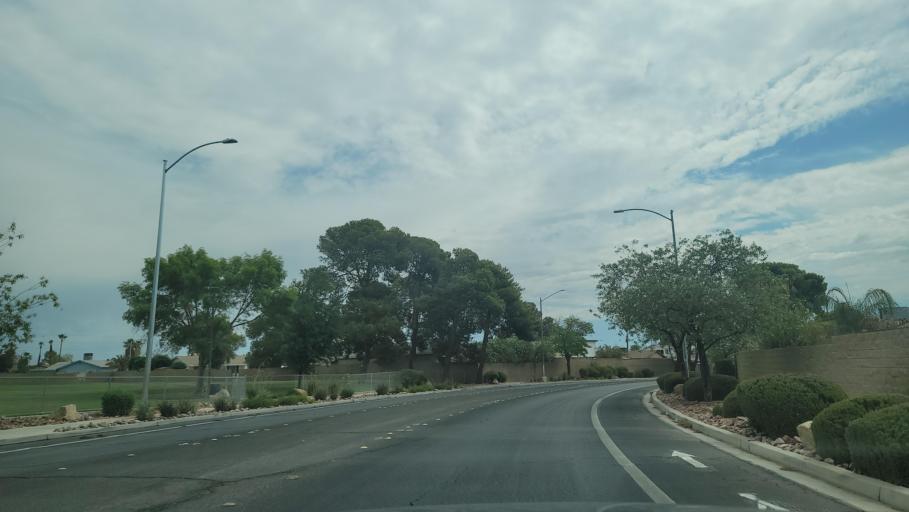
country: US
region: Nevada
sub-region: Clark County
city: Spring Valley
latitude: 36.1103
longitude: -115.2476
